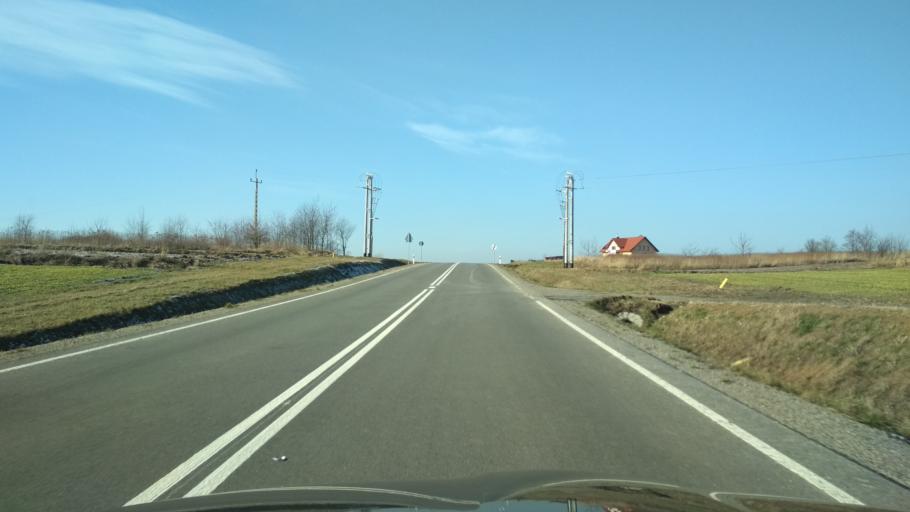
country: PL
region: Subcarpathian Voivodeship
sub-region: Powiat ropczycko-sedziszowski
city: Sedziszow Malopolski
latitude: 50.0763
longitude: 21.7269
